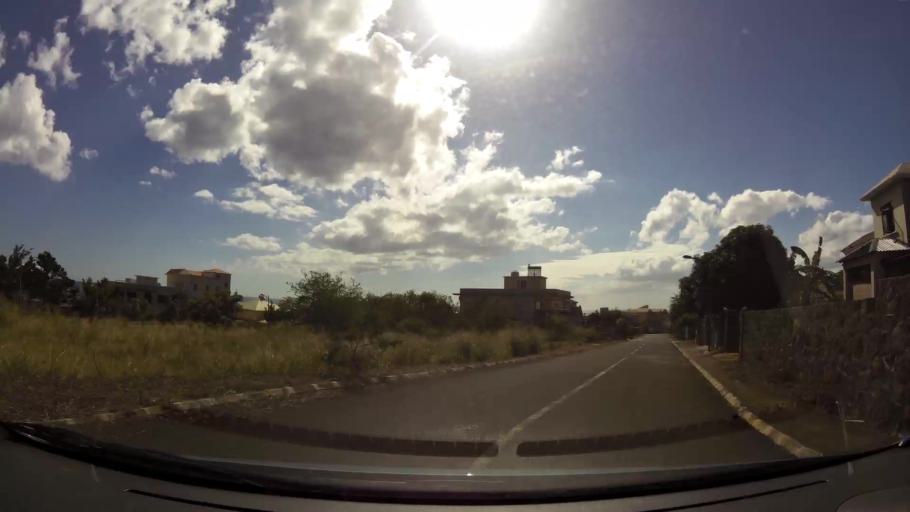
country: MU
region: Black River
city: Albion
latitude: -20.2183
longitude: 57.4124
